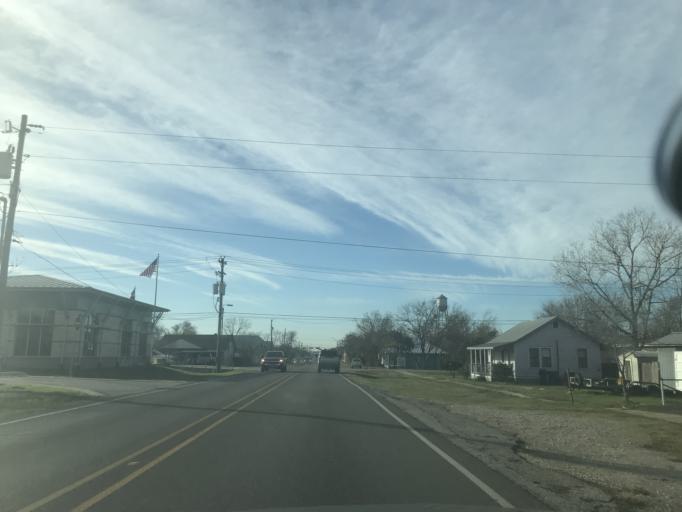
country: US
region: Texas
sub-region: Travis County
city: Manor
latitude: 30.3435
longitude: -97.5572
